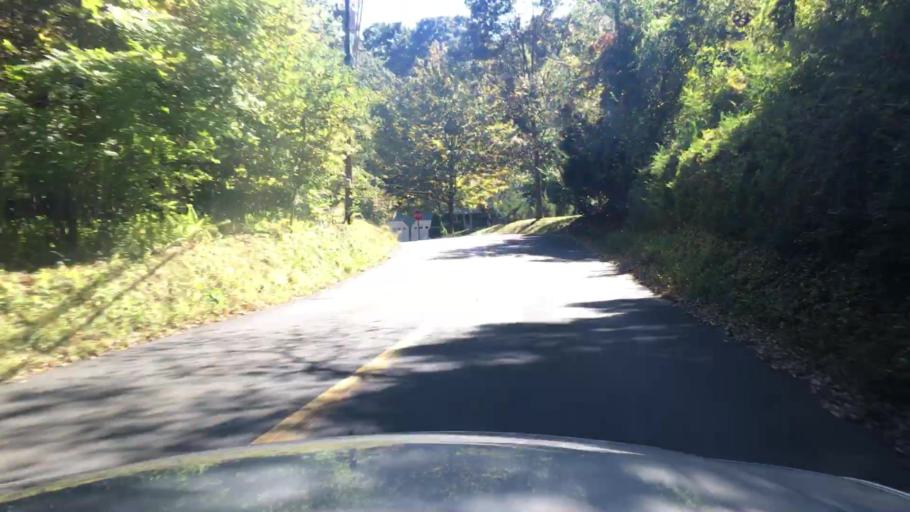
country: US
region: Connecticut
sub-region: Middlesex County
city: Essex Village
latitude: 41.3603
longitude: -72.4059
